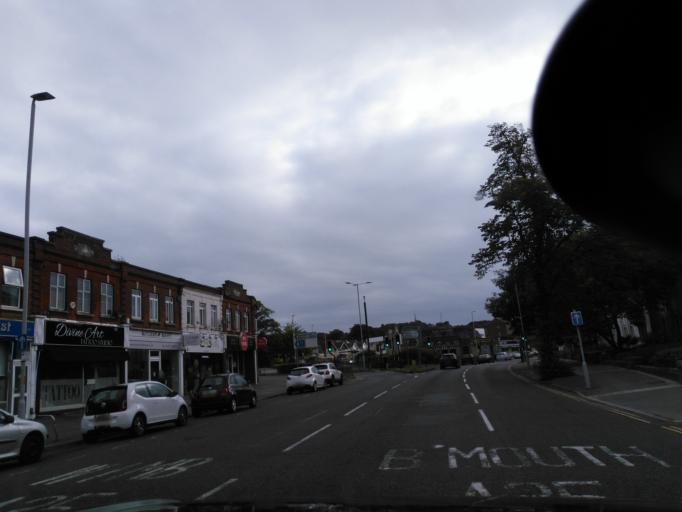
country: GB
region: England
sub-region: Dorset
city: Parkstone
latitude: 50.7229
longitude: -1.9632
